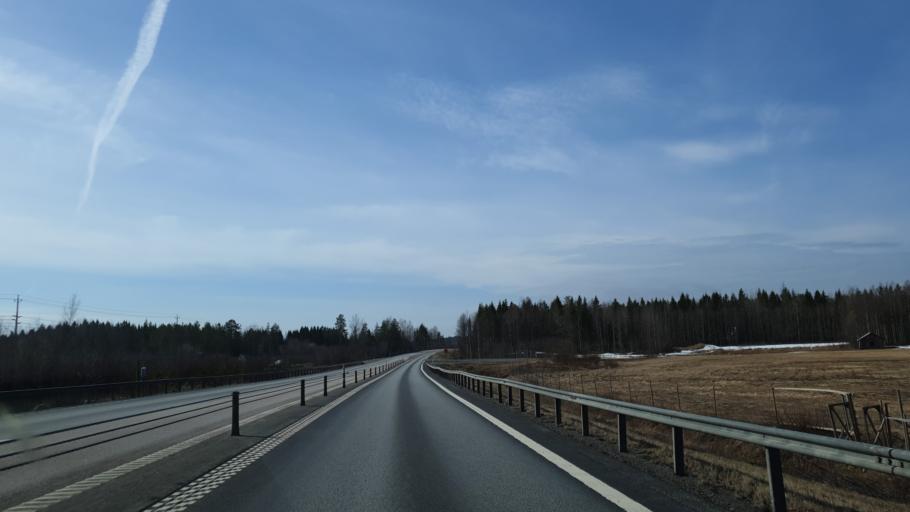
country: SE
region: Vaesterbotten
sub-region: Nordmalings Kommun
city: Nordmaling
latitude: 63.5060
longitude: 19.3477
